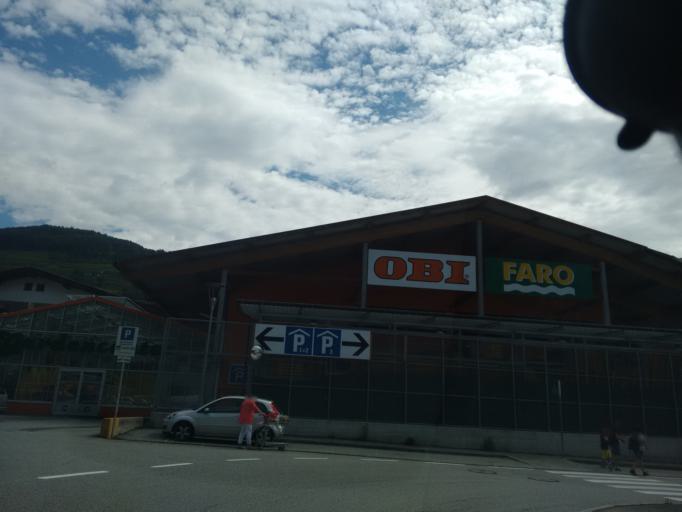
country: IT
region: Trentino-Alto Adige
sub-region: Bolzano
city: Leone-Santa Elisabetta
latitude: 46.7308
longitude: 11.6517
